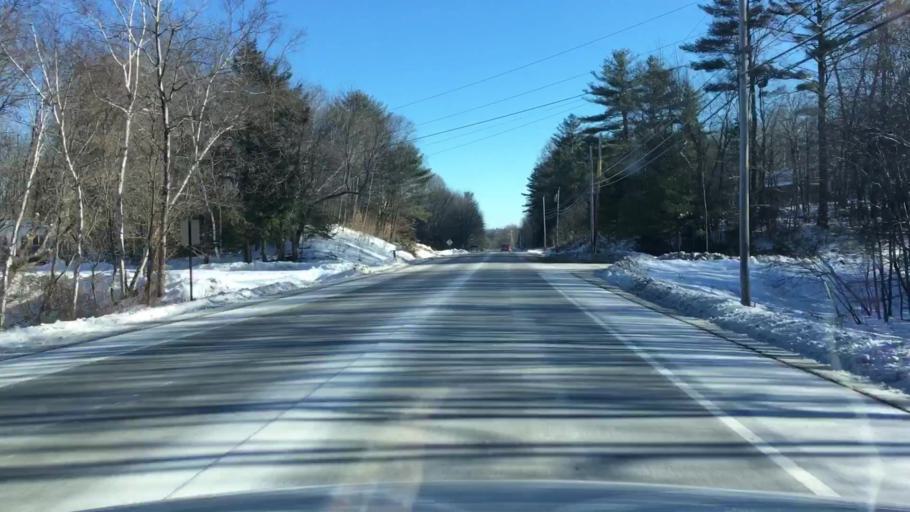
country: US
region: Maine
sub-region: Kennebec County
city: Readfield
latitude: 44.3907
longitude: -69.9819
